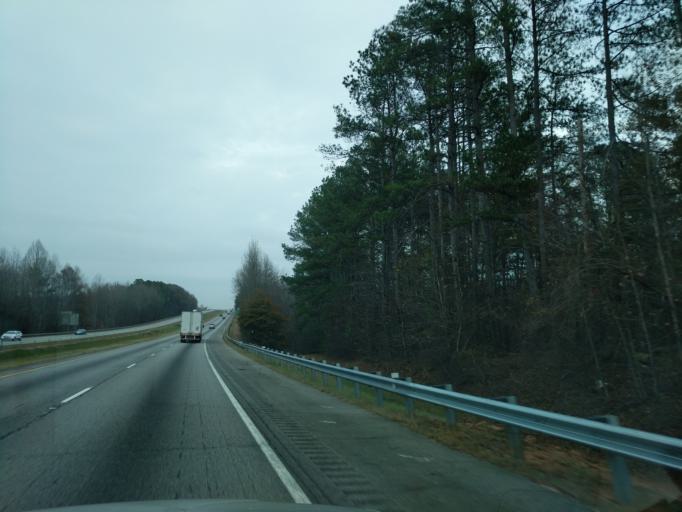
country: US
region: Georgia
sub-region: Franklin County
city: Carnesville
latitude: 34.3835
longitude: -83.2455
